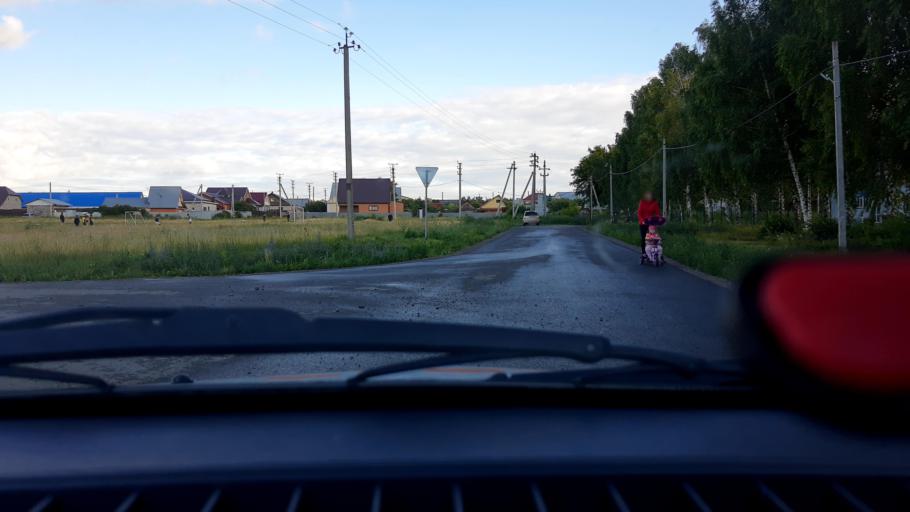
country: RU
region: Bashkortostan
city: Avdon
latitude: 54.4977
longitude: 55.8998
